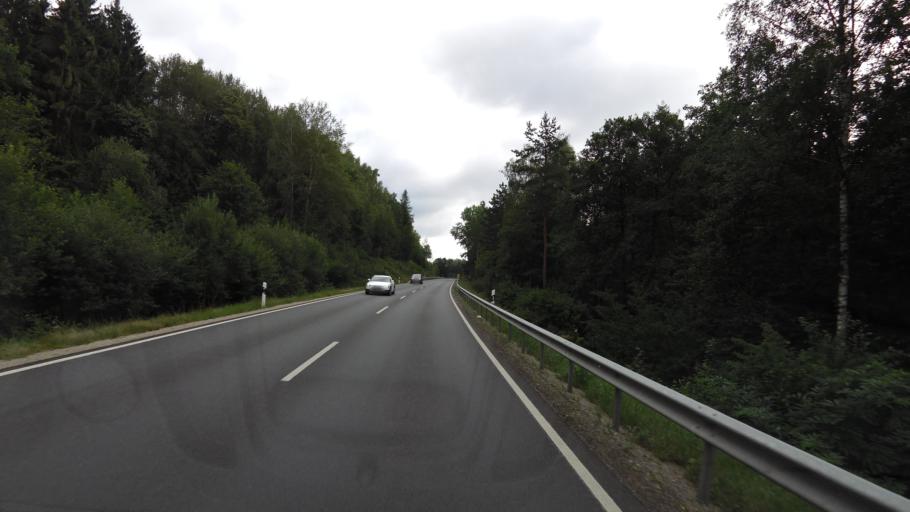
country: DE
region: Bavaria
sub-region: Lower Bavaria
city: Loitzendorf
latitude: 49.1015
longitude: 12.6476
